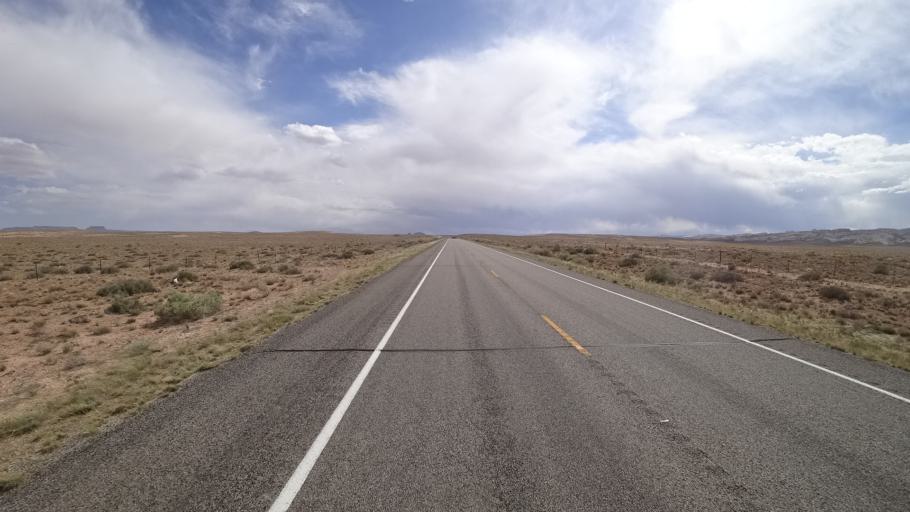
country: US
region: Utah
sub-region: Emery County
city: Castle Dale
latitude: 38.6868
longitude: -110.5261
